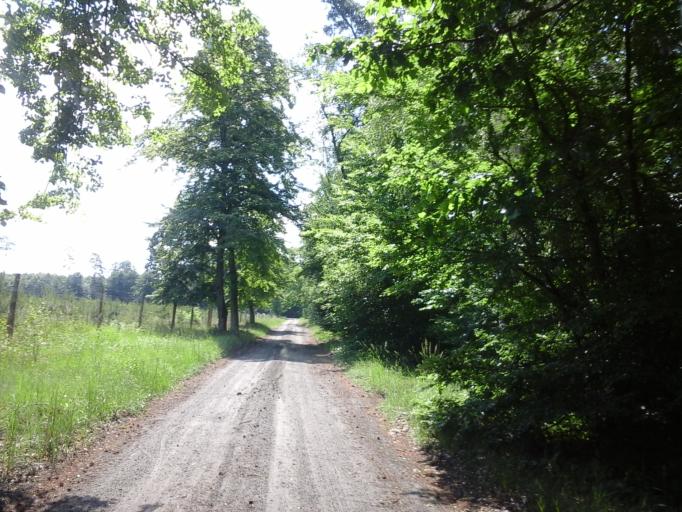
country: PL
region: West Pomeranian Voivodeship
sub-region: Powiat choszczenski
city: Bierzwnik
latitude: 53.0808
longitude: 15.7228
